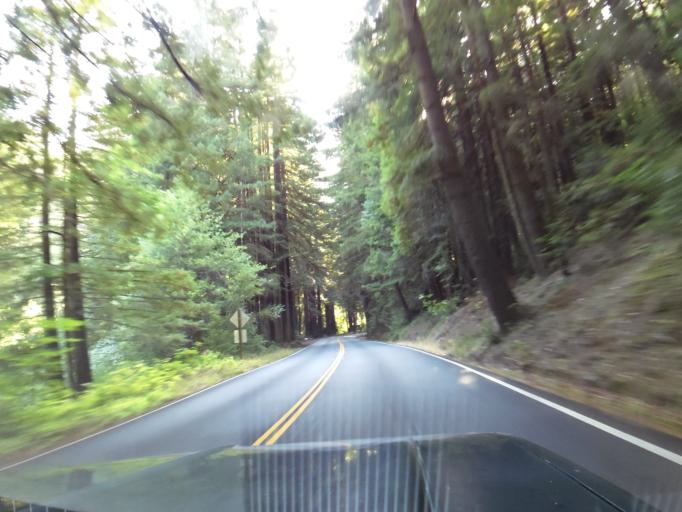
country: US
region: California
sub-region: Mendocino County
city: Boonville
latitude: 39.1565
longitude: -123.6251
